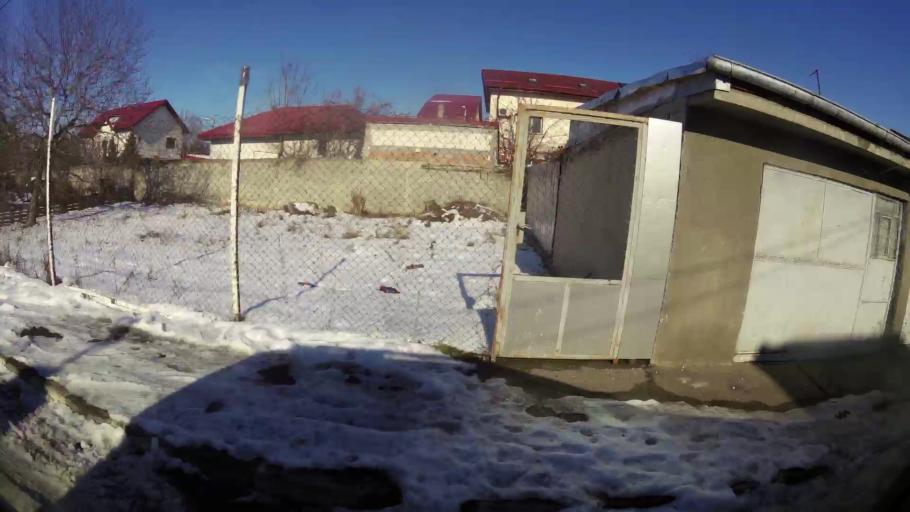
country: RO
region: Ilfov
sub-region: Comuna Magurele
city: Magurele
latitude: 44.3969
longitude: 26.0495
